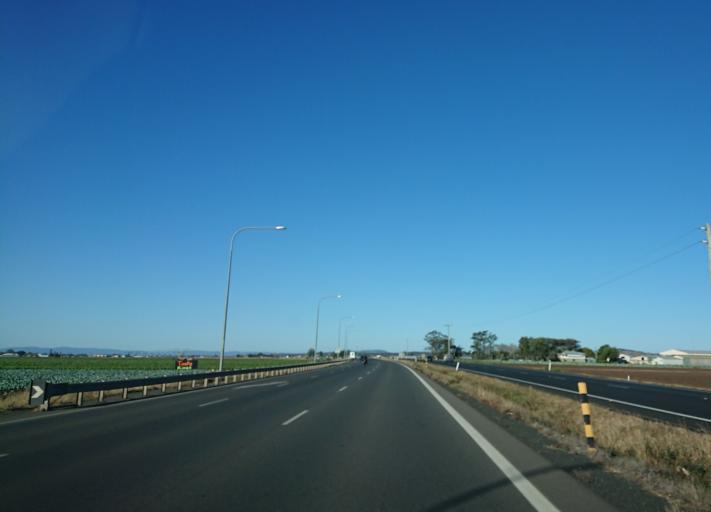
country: AU
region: Queensland
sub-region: Lockyer Valley
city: Gatton
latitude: -27.5444
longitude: 152.3476
